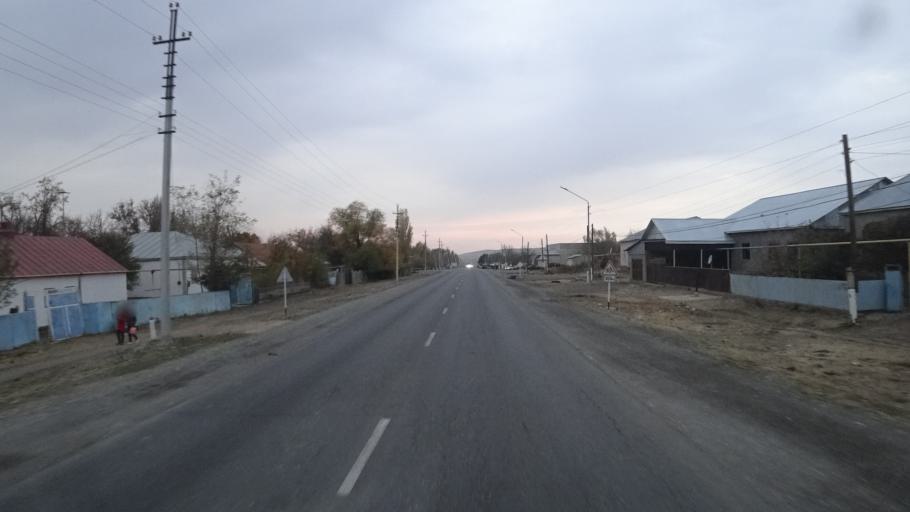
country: KZ
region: Ongtustik Qazaqstan
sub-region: Tulkibas Audany
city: Zhabagly
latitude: 42.5115
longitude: 70.5641
